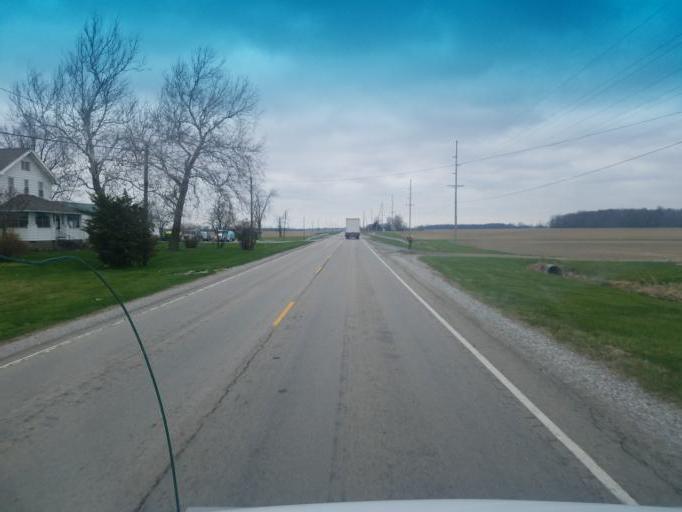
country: US
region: Ohio
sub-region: Paulding County
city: Antwerp
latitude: 41.2185
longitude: -84.7509
